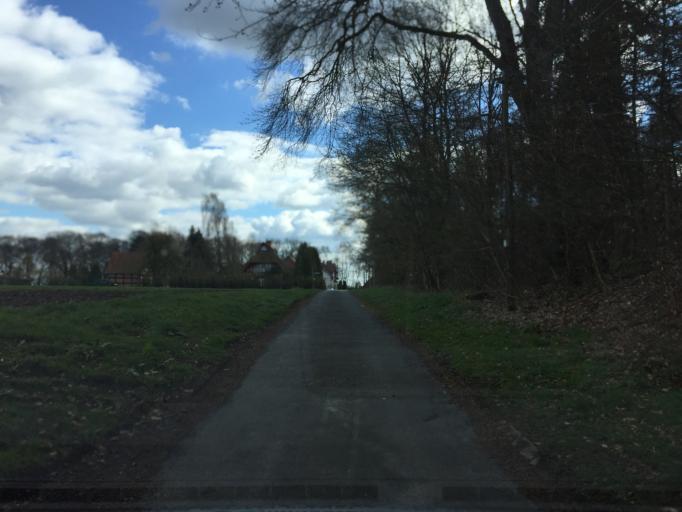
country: DE
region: Lower Saxony
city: Bruchhausen-Vilsen
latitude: 52.8014
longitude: 8.9971
